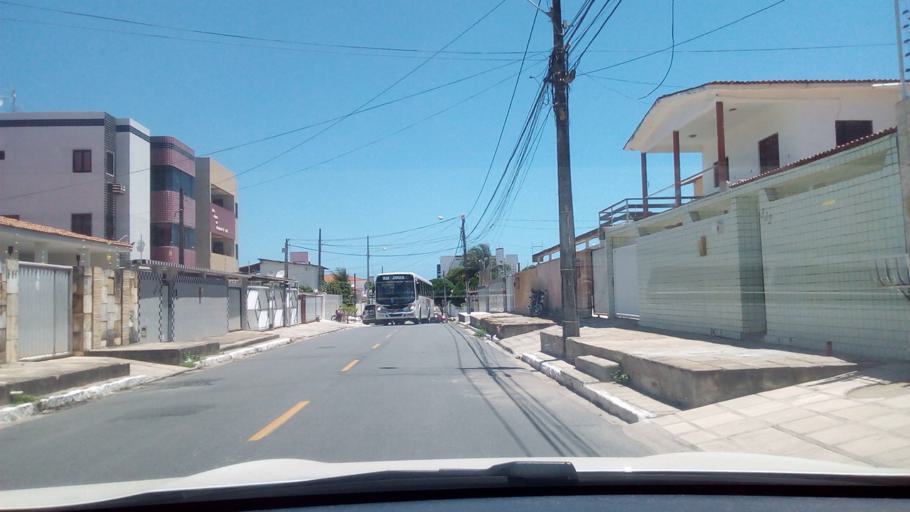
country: BR
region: Paraiba
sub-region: Joao Pessoa
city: Joao Pessoa
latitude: -7.1575
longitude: -34.8357
